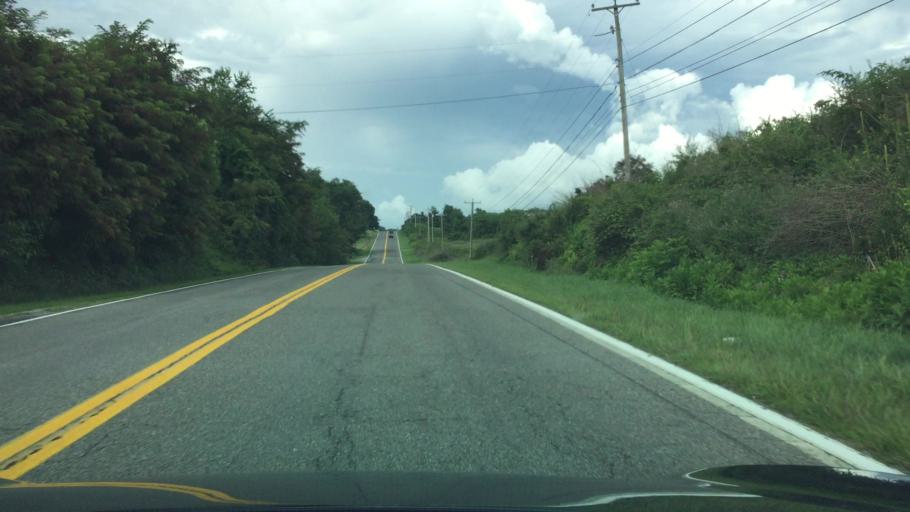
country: US
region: Virginia
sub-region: Pulaski County
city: Pulaski
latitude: 36.9505
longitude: -80.8891
